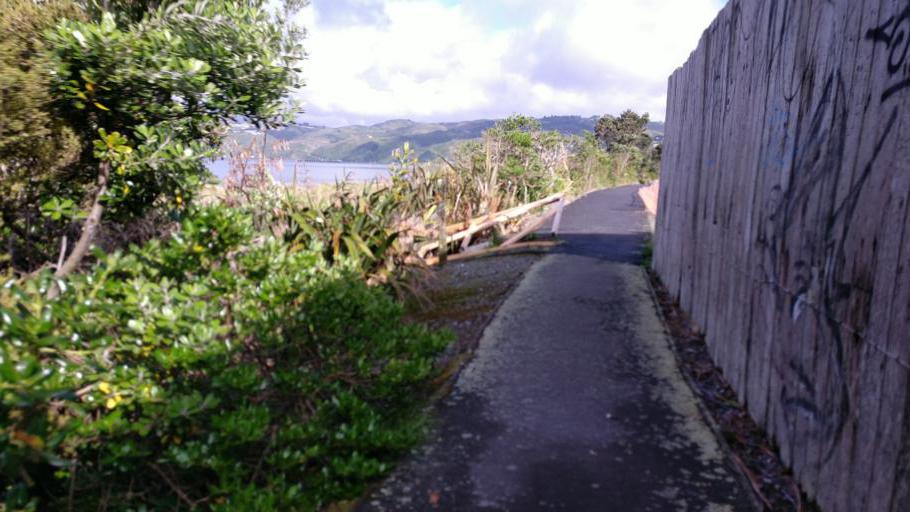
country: NZ
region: Wellington
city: Petone
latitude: -41.2329
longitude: 174.8907
